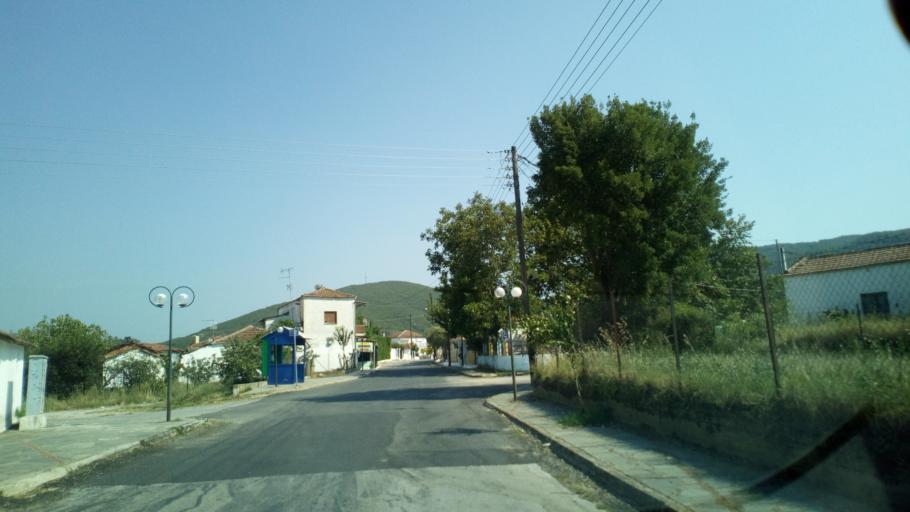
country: GR
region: Central Macedonia
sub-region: Nomos Chalkidikis
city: Galatista
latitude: 40.5565
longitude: 23.3009
